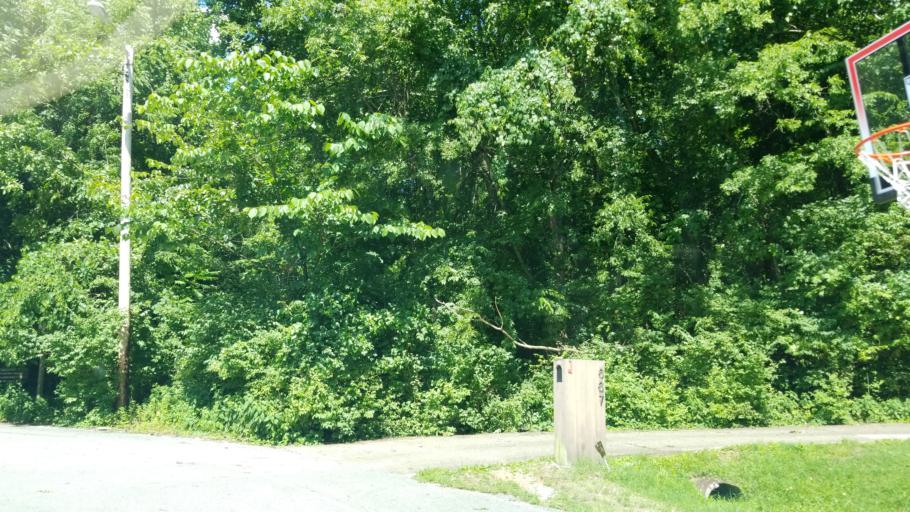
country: US
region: Tennessee
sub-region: Williamson County
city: Brentwood
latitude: 36.0492
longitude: -86.7896
